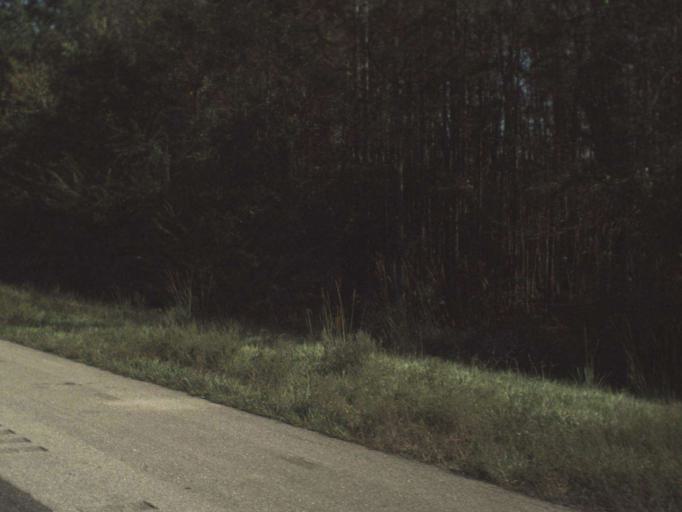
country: US
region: Florida
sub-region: Washington County
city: Chipley
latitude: 30.7462
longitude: -85.4354
